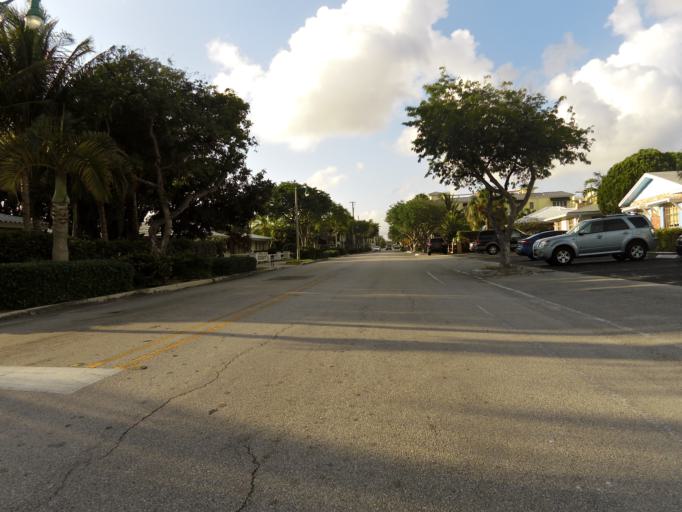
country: US
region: Florida
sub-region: Broward County
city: Lauderdale-by-the-Sea
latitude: 26.1878
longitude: -80.0984
